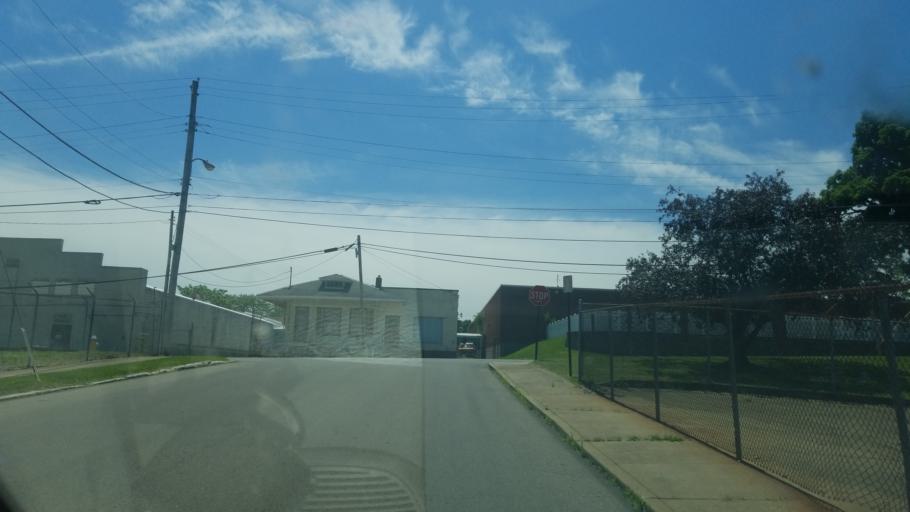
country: US
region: Ohio
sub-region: Richland County
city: Mansfield
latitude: 40.7611
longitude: -82.5100
